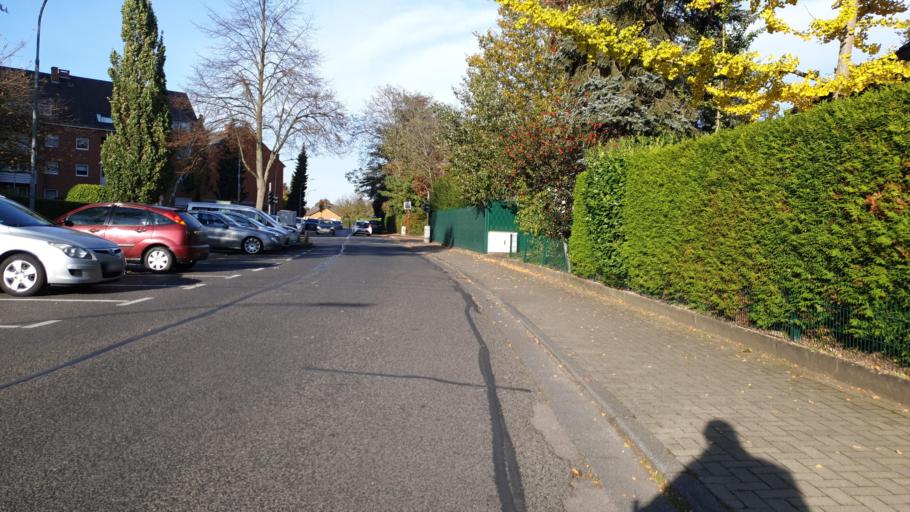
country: DE
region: North Rhine-Westphalia
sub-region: Regierungsbezirk Koln
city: Kerpen
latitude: 50.9076
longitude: 6.6829
